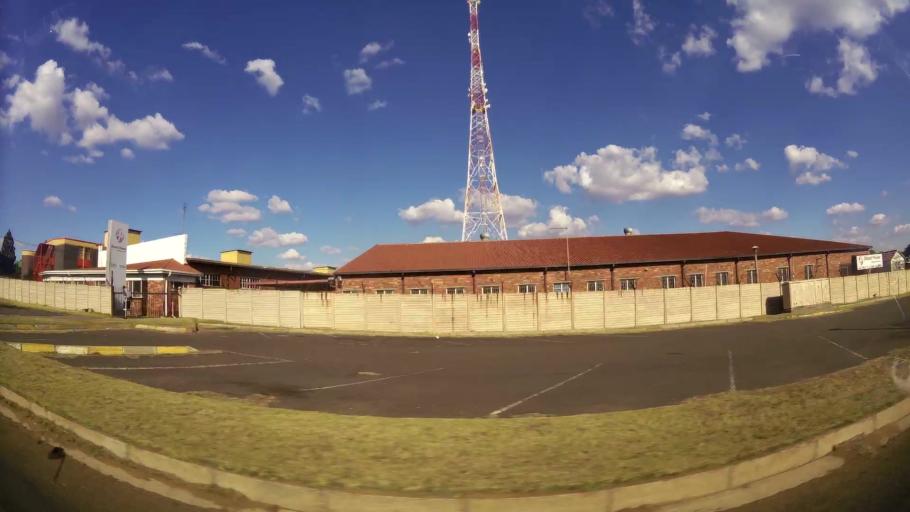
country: ZA
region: Mpumalanga
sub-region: Nkangala District Municipality
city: Witbank
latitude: -25.9015
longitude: 29.2270
